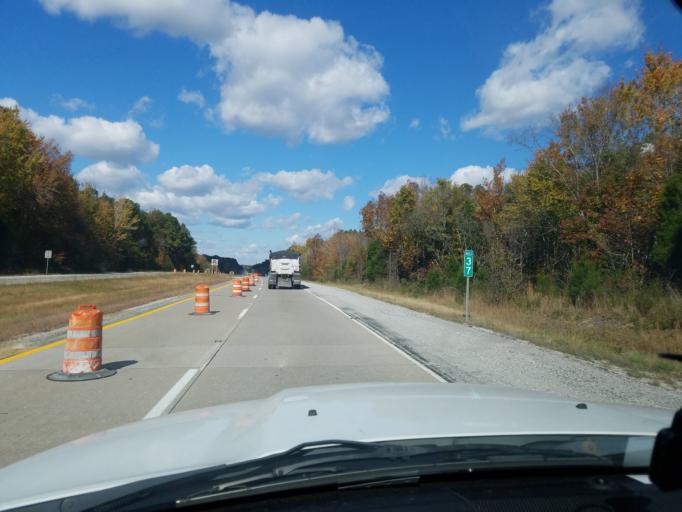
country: US
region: Kentucky
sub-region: Ohio County
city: Oak Grove
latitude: 37.3127
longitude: -86.7386
